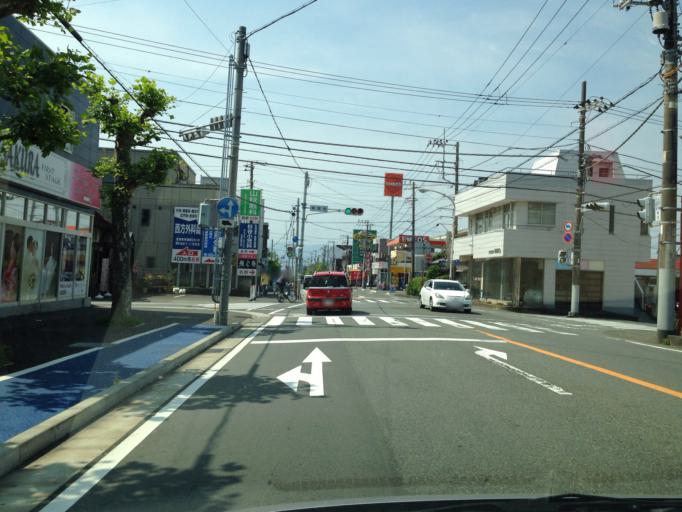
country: JP
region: Shizuoka
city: Numazu
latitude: 35.1198
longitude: 138.8677
